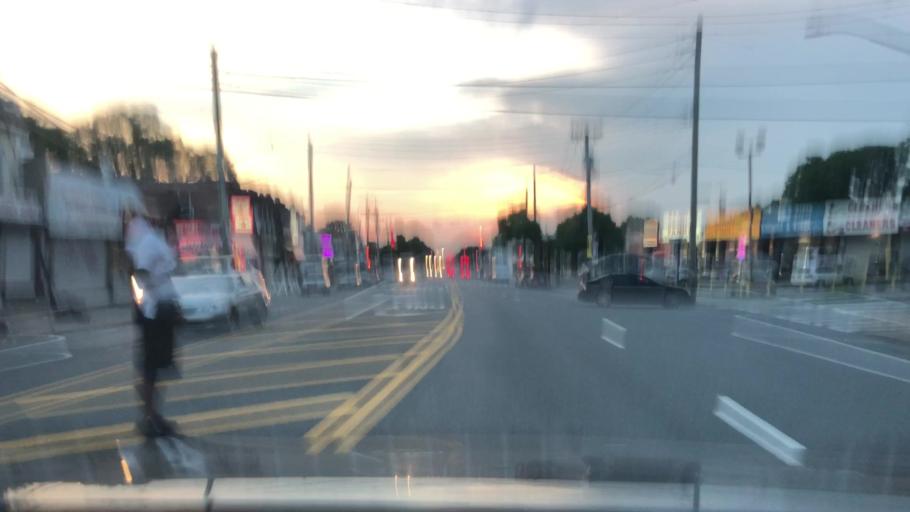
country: US
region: New York
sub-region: Queens County
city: Jamaica
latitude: 40.6734
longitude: -73.7903
